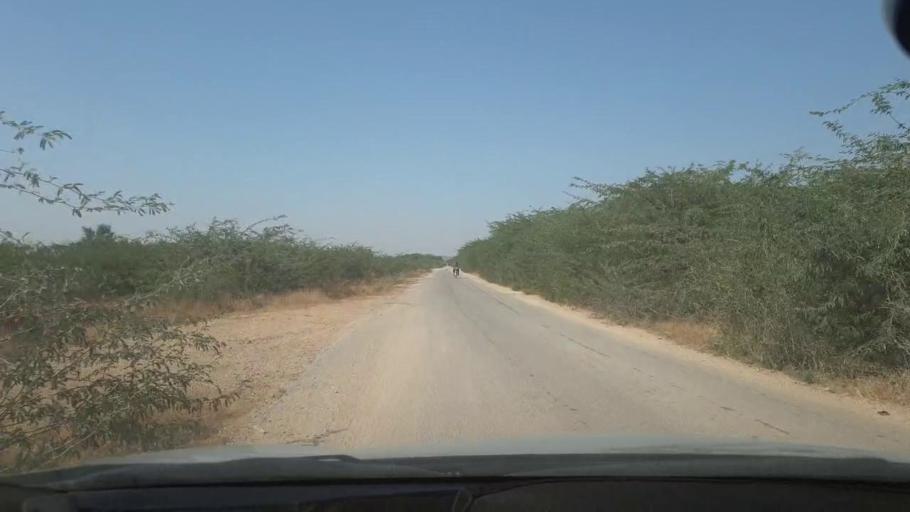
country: PK
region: Sindh
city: Malir Cantonment
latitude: 25.1472
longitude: 67.1661
